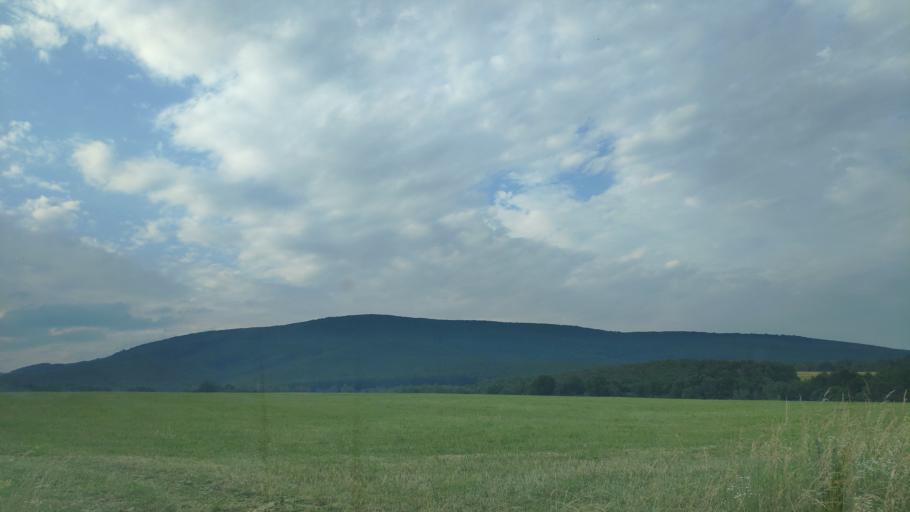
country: SK
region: Kosicky
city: Moldava nad Bodvou
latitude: 48.7090
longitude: 20.9936
